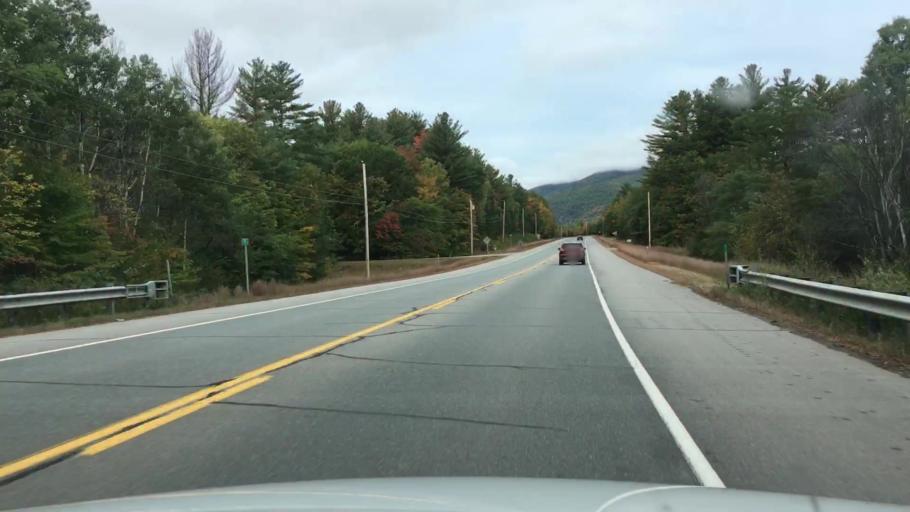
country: US
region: New Hampshire
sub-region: Coos County
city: Gorham
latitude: 44.3940
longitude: -71.0510
